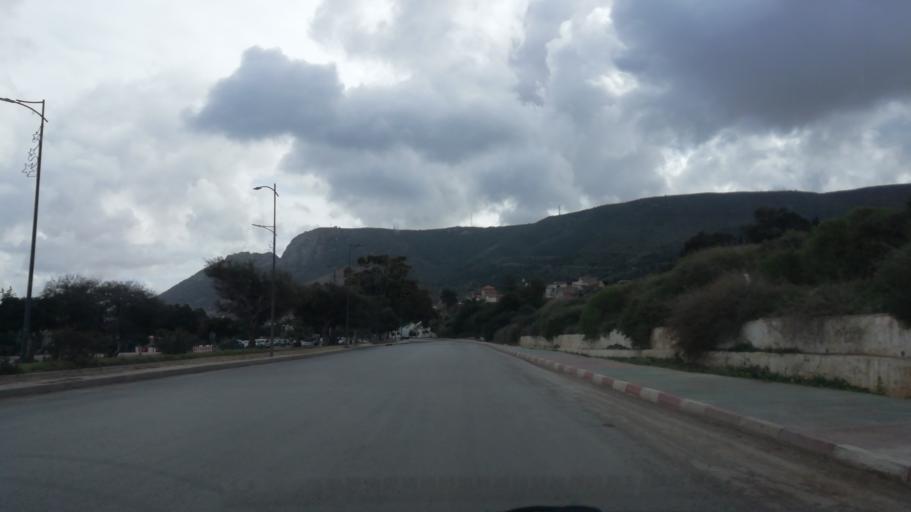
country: DZ
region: Oran
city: Mers el Kebir
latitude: 35.7179
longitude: -0.6979
